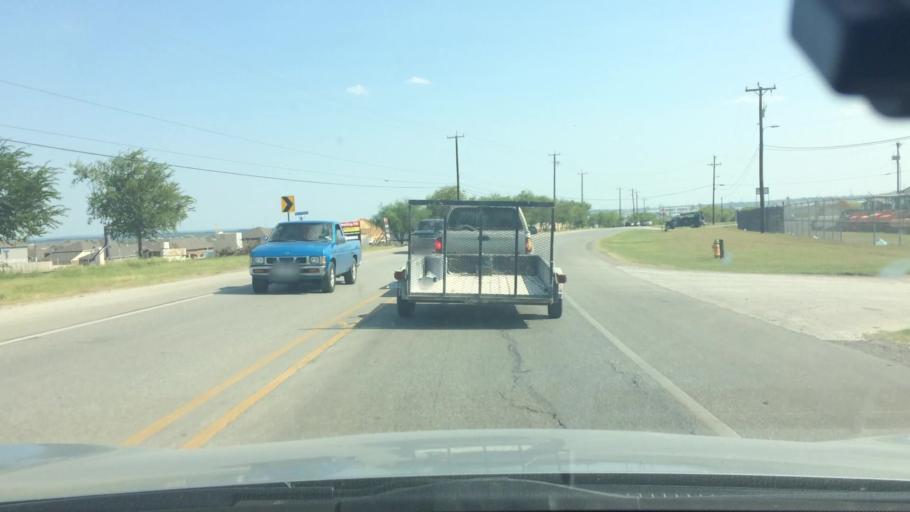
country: US
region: Texas
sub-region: Bexar County
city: Converse
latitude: 29.4731
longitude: -98.3136
